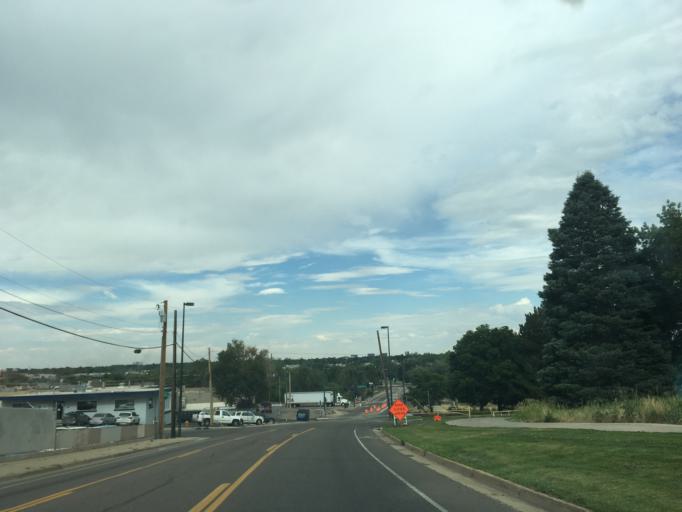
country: US
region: Colorado
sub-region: Arapahoe County
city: Englewood
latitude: 39.6894
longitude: -105.0026
